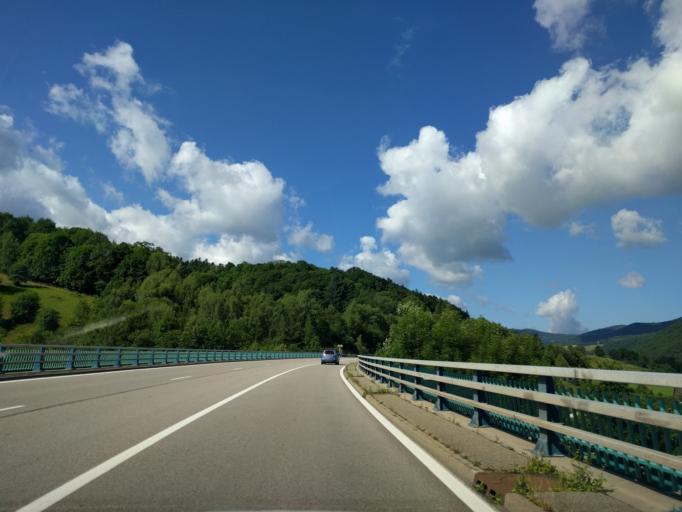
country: FR
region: Alsace
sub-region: Departement du Haut-Rhin
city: Sainte-Croix-aux-Mines
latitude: 48.2598
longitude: 7.2316
